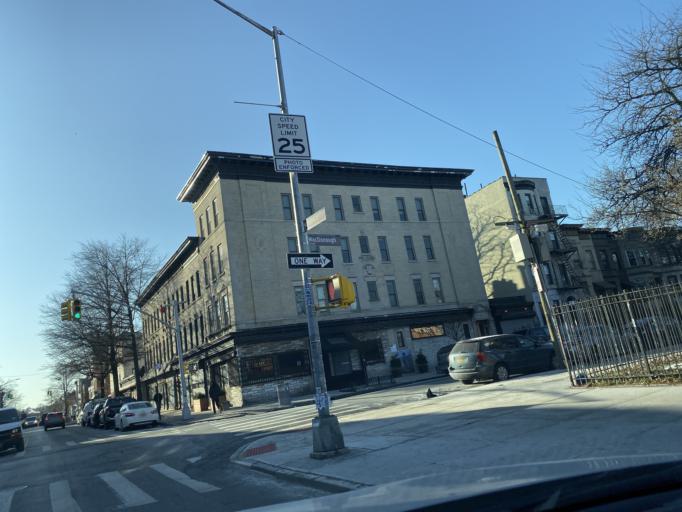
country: US
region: New York
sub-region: Kings County
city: Brooklyn
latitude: 40.6829
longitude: -73.9291
